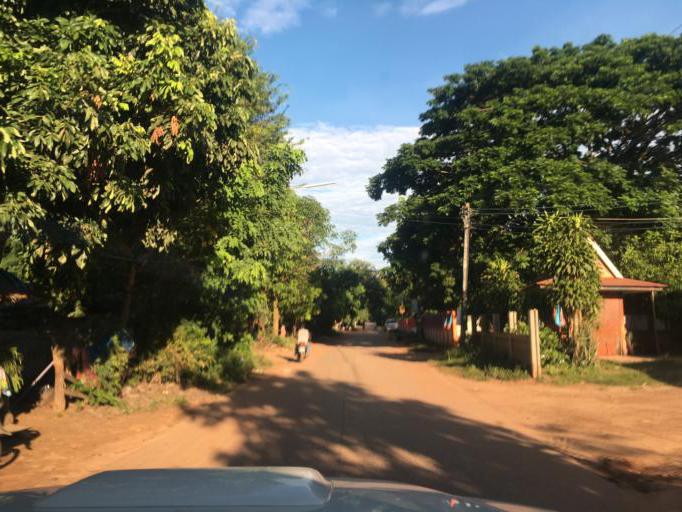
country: TH
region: Changwat Udon Thani
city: Nong Saeng
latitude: 17.2794
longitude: 102.7023
